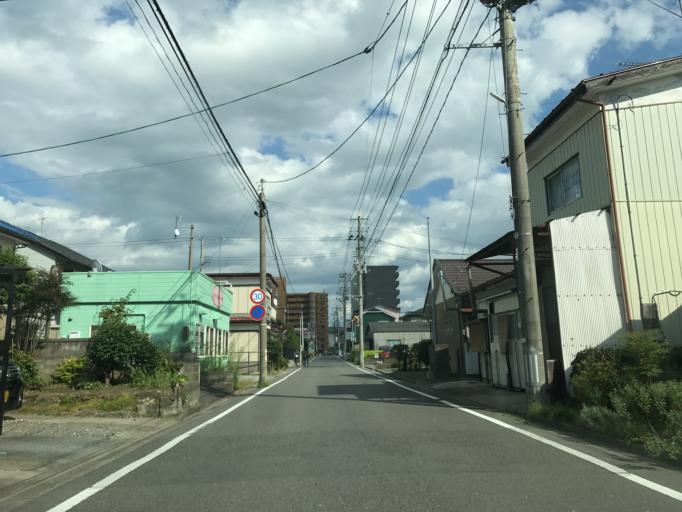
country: JP
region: Fukushima
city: Koriyama
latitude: 37.4066
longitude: 140.3861
